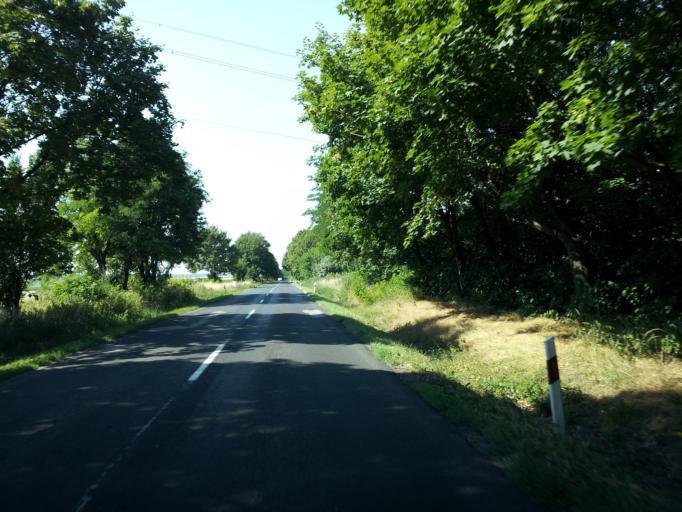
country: HU
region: Fejer
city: Lovasbereny
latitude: 47.3312
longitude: 18.5754
